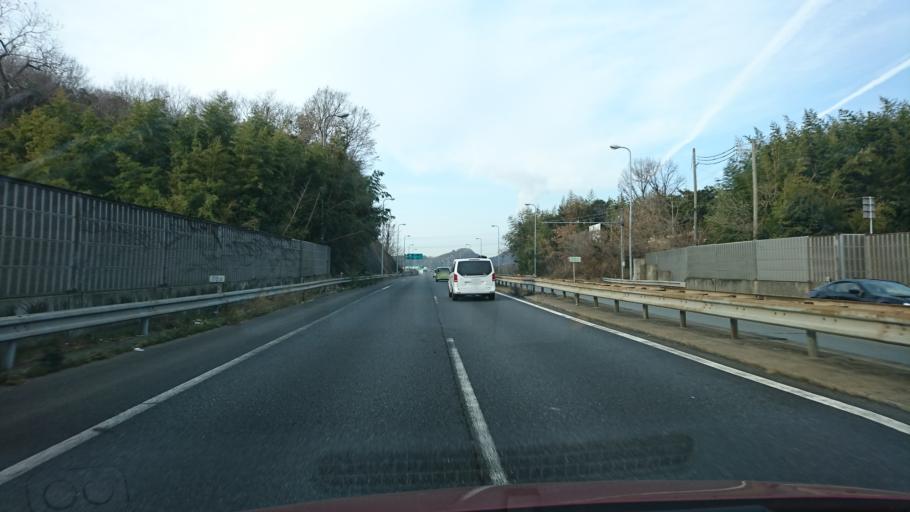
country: JP
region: Hyogo
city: Kakogawacho-honmachi
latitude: 34.7876
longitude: 134.7882
